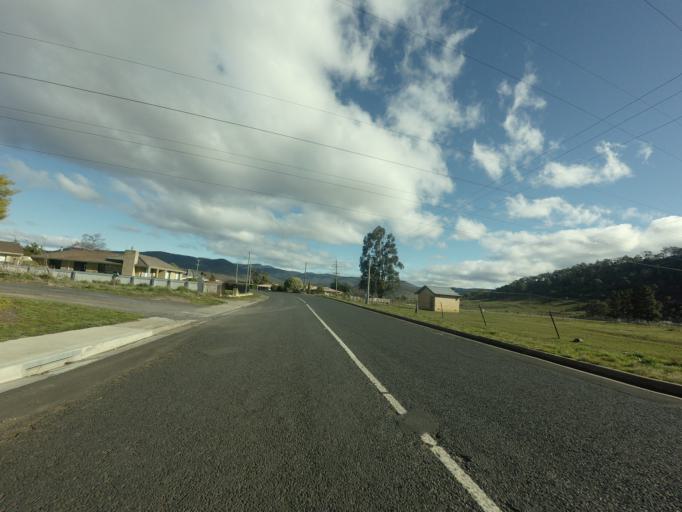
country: AU
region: Tasmania
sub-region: Derwent Valley
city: New Norfolk
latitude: -42.7584
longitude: 147.0479
